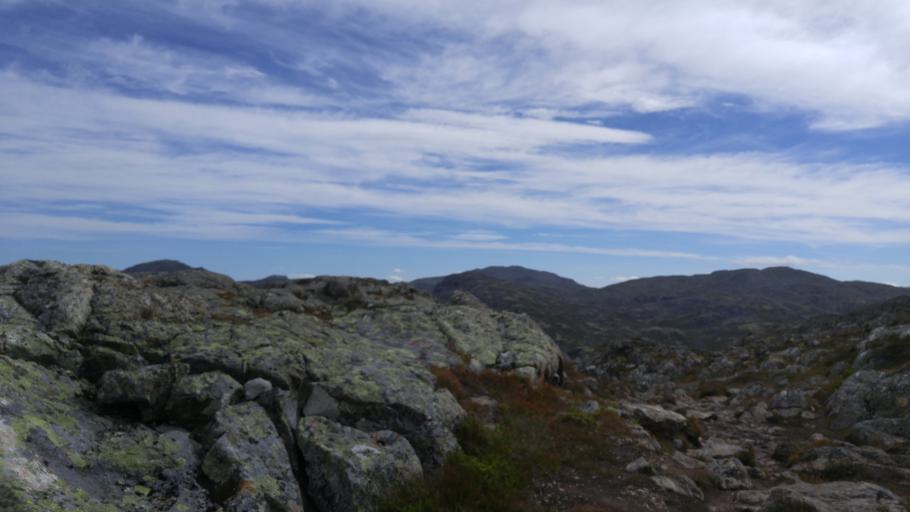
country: NO
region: Buskerud
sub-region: Hemsedal
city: Hemsedal
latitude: 60.8539
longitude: 8.4593
